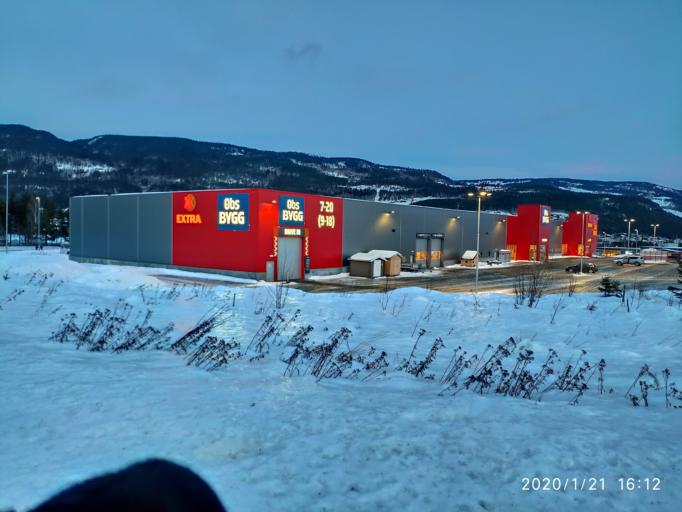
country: NO
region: Oppland
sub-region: Nord-Fron
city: Vinstra
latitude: 61.5942
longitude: 9.7233
